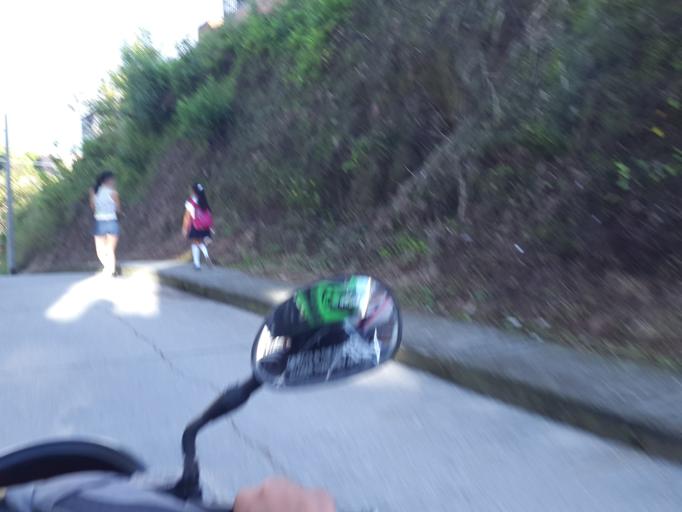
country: CO
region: Quindio
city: Montenegro
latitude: 4.5640
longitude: -75.7487
